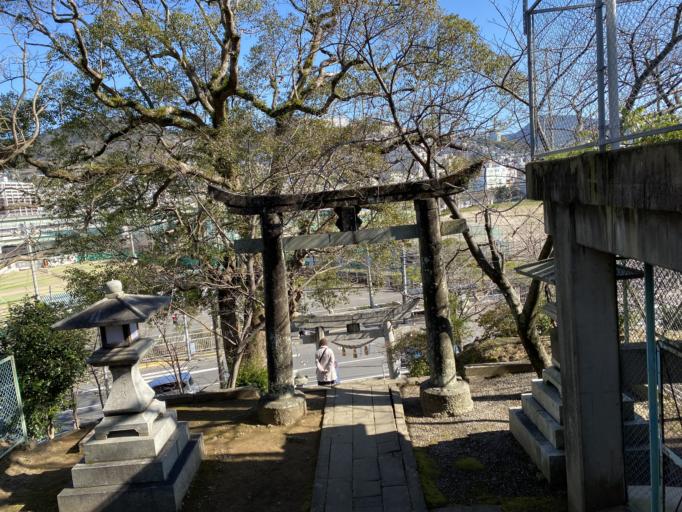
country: JP
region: Nagasaki
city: Nagasaki-shi
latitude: 32.7583
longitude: 129.8604
